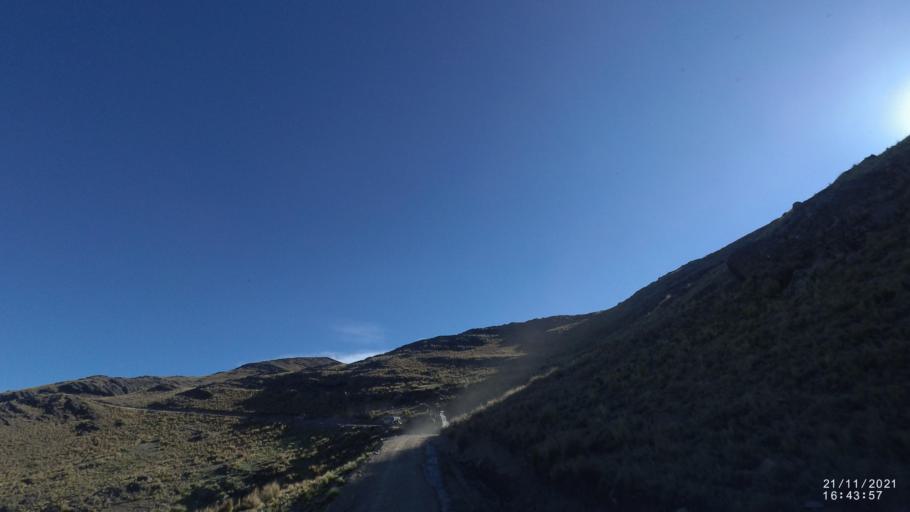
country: BO
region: Cochabamba
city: Cochabamba
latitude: -17.0722
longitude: -66.2579
